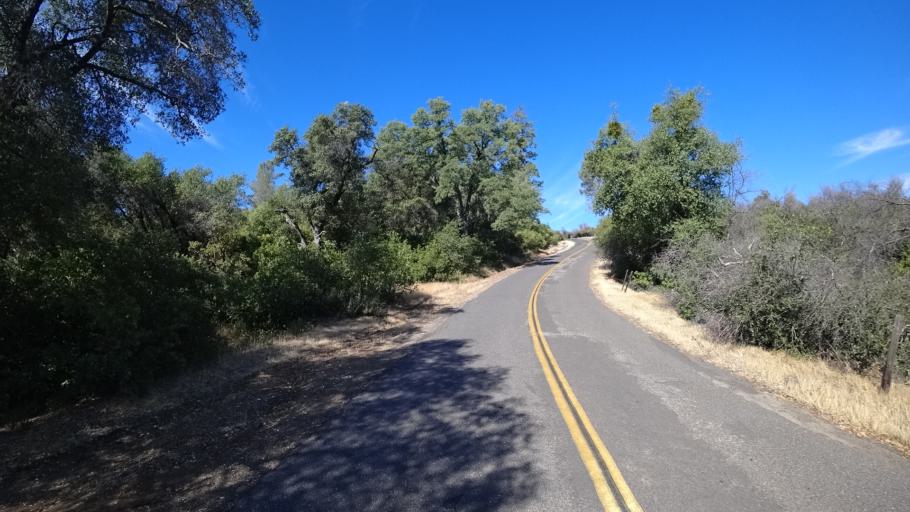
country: US
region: California
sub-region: Calaveras County
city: Mountain Ranch
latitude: 38.1644
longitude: -120.5467
